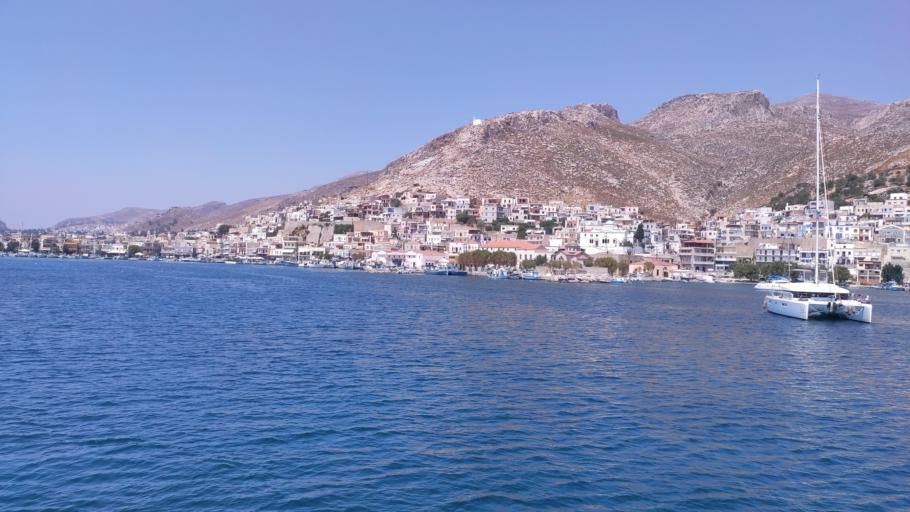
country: GR
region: South Aegean
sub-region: Nomos Dodekanisou
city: Kalymnos
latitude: 36.9489
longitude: 26.9909
